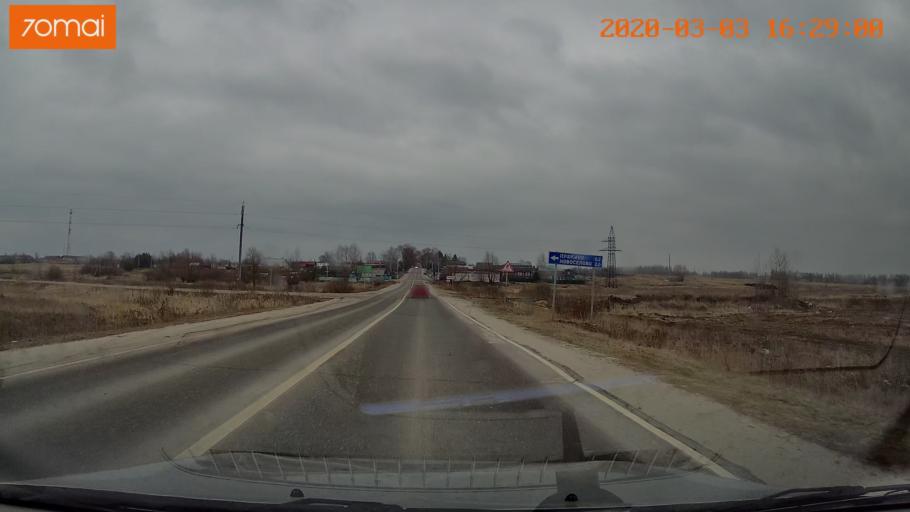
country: RU
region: Moskovskaya
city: Konobeyevo
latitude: 55.4380
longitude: 38.6960
